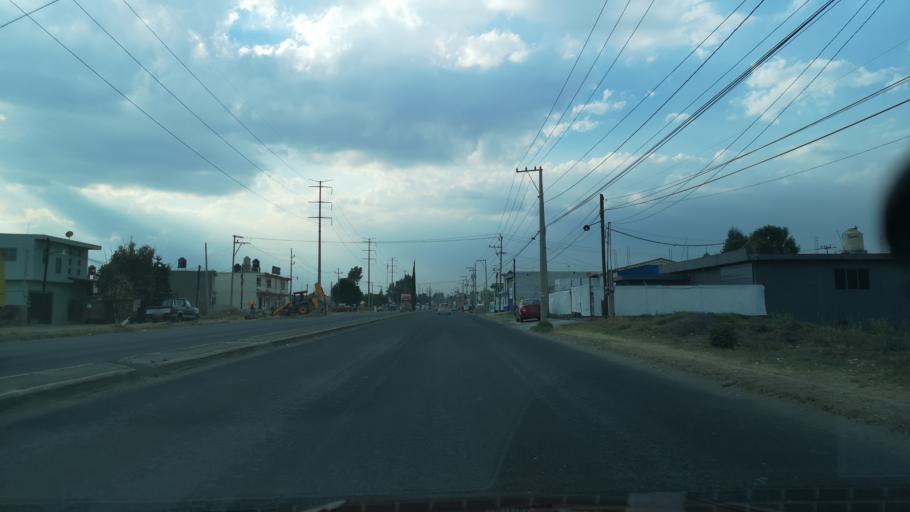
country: MX
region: Puebla
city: Cuanala
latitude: 19.0900
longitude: -98.3356
